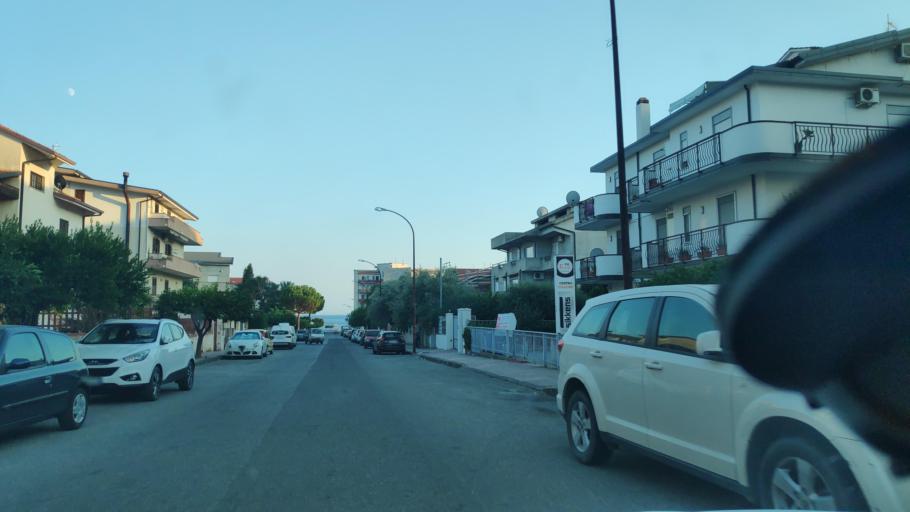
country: IT
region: Calabria
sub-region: Provincia di Reggio Calabria
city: Roccella Ionica
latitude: 38.3206
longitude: 16.3950
